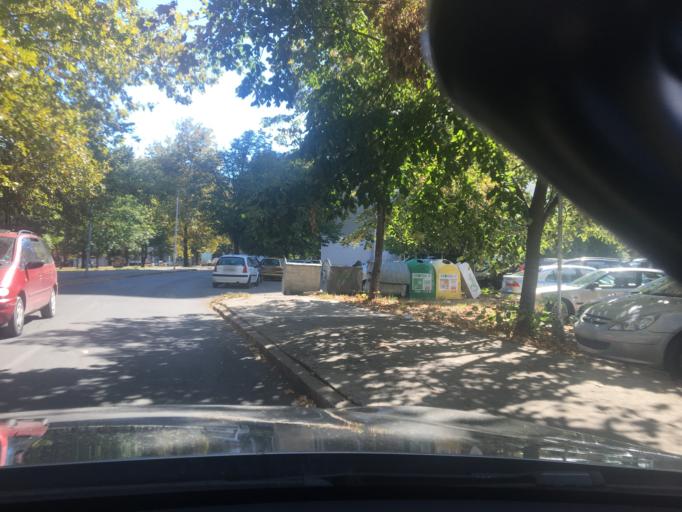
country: BG
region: Burgas
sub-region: Obshtina Burgas
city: Burgas
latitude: 42.5054
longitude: 27.4750
